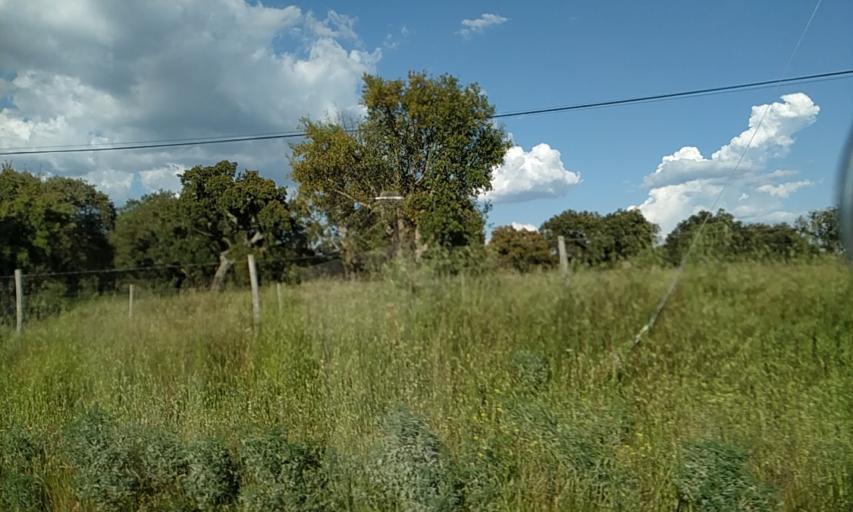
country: PT
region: Portalegre
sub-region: Portalegre
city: Urra
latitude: 39.1693
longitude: -7.4538
